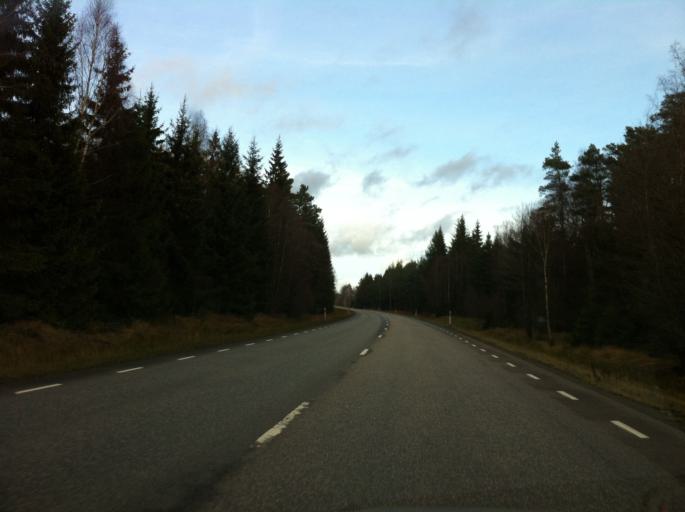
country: SE
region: Kronoberg
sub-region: Almhults Kommun
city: AElmhult
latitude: 56.5591
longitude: 14.1799
